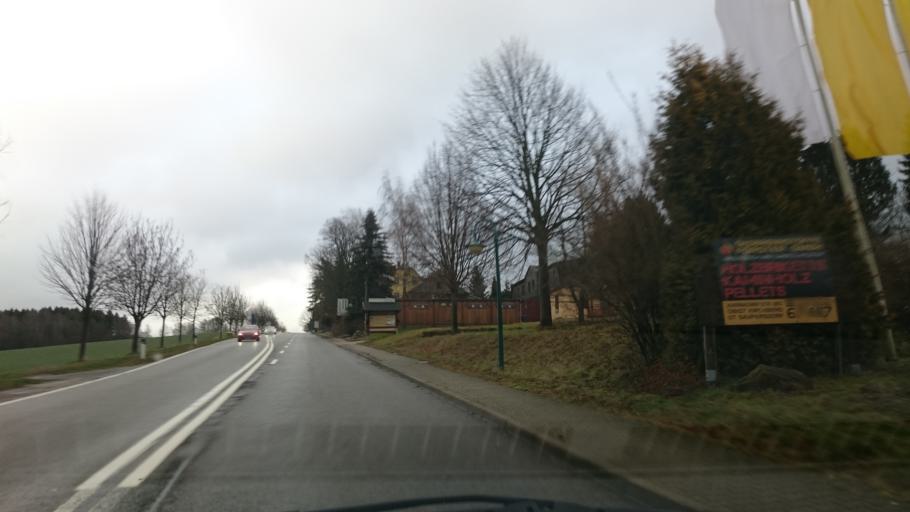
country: DE
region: Saxony
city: Wildenfels
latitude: 50.6139
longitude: 12.5858
